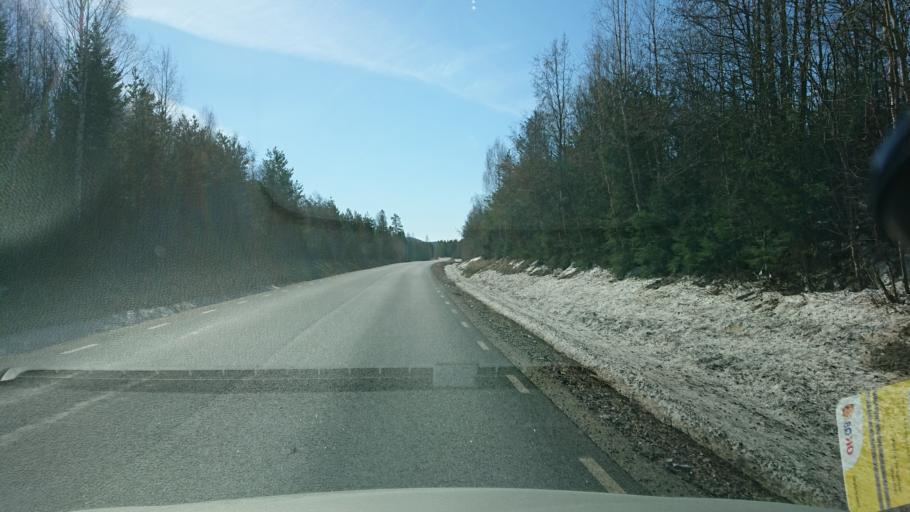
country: SE
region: Vaesterbotten
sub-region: Dorotea Kommun
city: Dorotea
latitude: 64.0902
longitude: 16.2600
